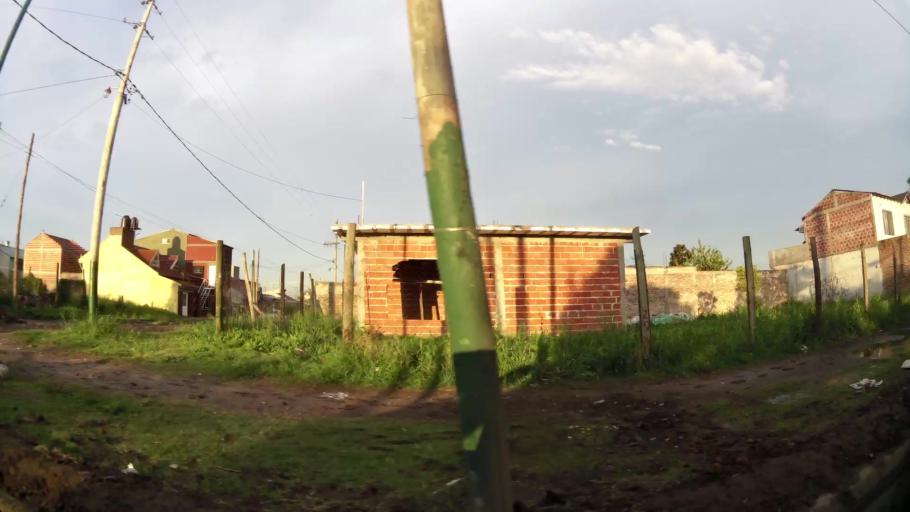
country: AR
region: Buenos Aires
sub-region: Partido de Almirante Brown
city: Adrogue
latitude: -34.7653
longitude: -58.3420
